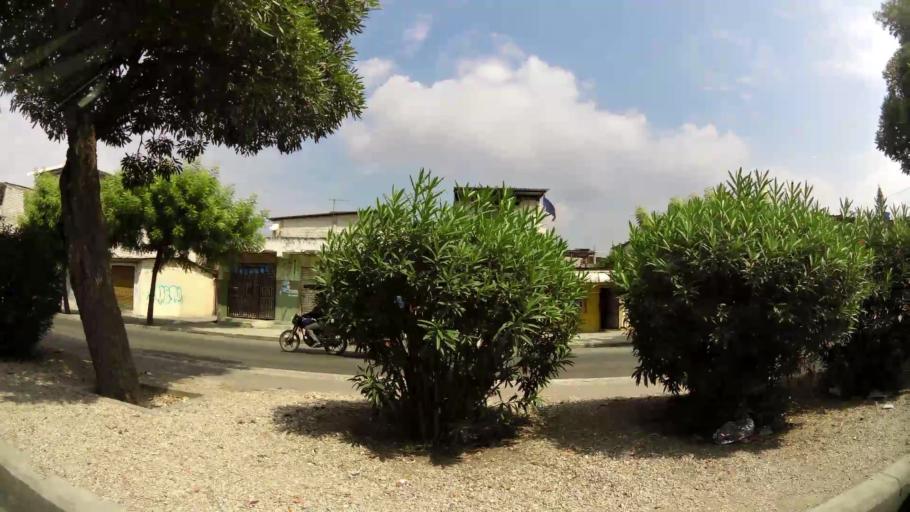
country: EC
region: Guayas
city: Guayaquil
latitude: -2.2653
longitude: -79.8778
